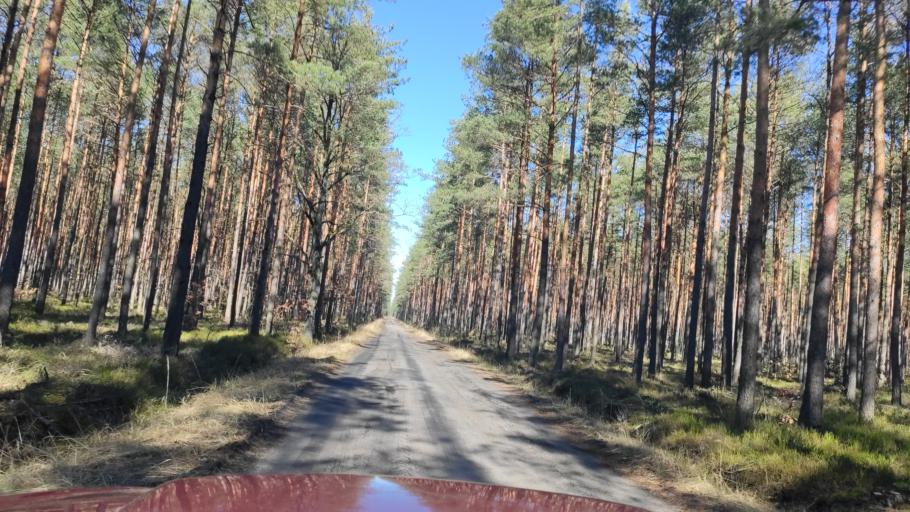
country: PL
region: Masovian Voivodeship
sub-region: Powiat zwolenski
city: Zwolen
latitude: 51.4185
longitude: 21.5534
